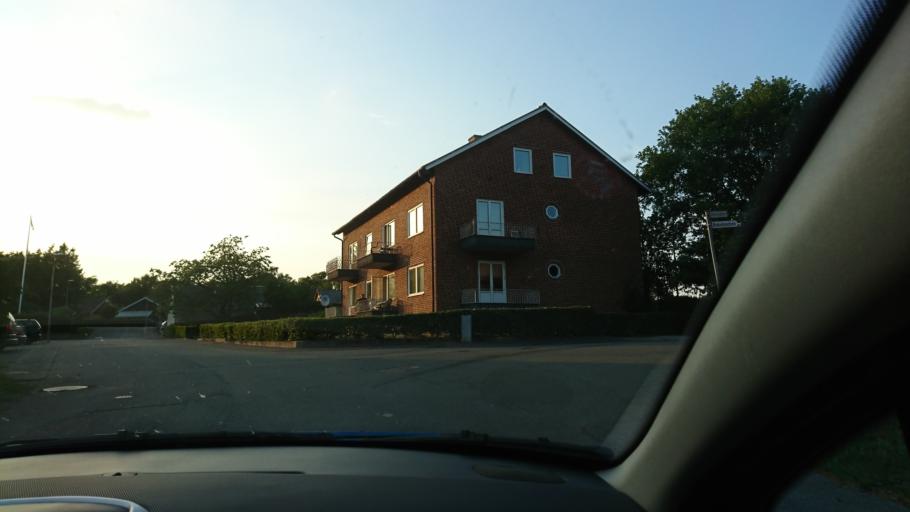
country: SE
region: Skane
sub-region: Simrishamns Kommun
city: Kivik
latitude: 55.6347
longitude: 14.1289
